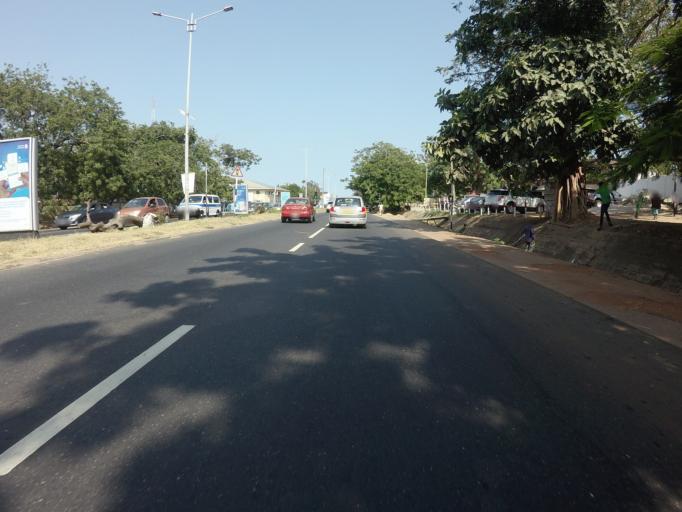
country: GH
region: Greater Accra
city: Accra
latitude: 5.5692
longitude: -0.1851
